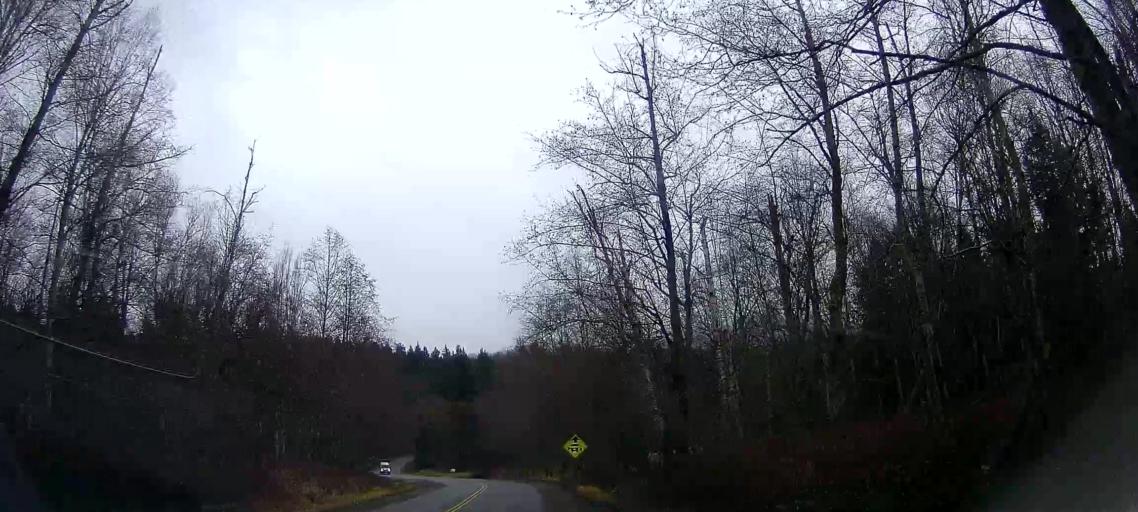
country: US
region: Washington
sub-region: Skagit County
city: Mount Vernon
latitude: 48.3813
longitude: -122.3049
